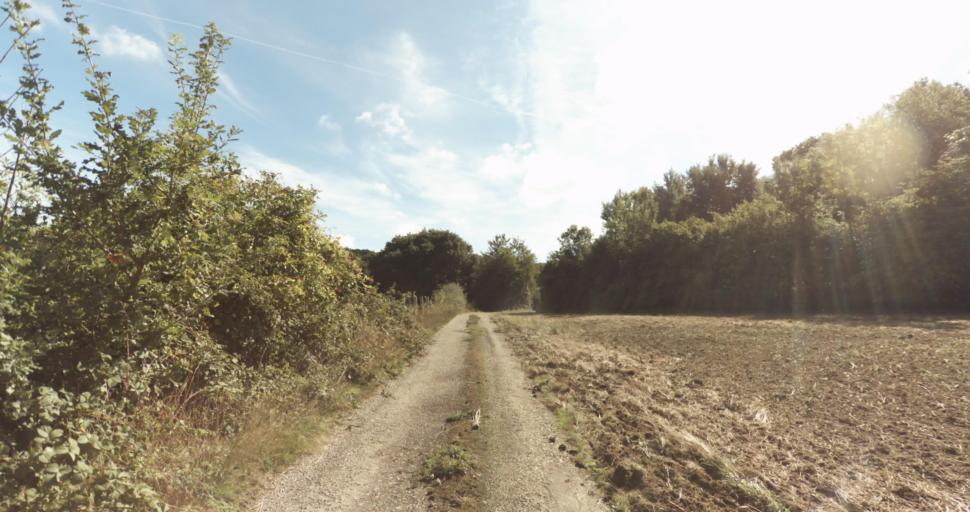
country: FR
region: Lower Normandy
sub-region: Departement de l'Orne
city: Vimoutiers
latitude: 48.9307
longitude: 0.3086
